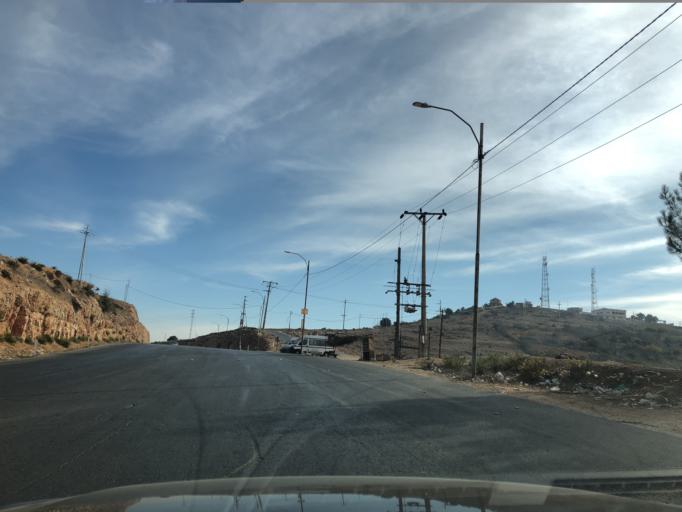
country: JO
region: Irbid
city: `Anjarah
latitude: 32.3052
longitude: 35.7753
